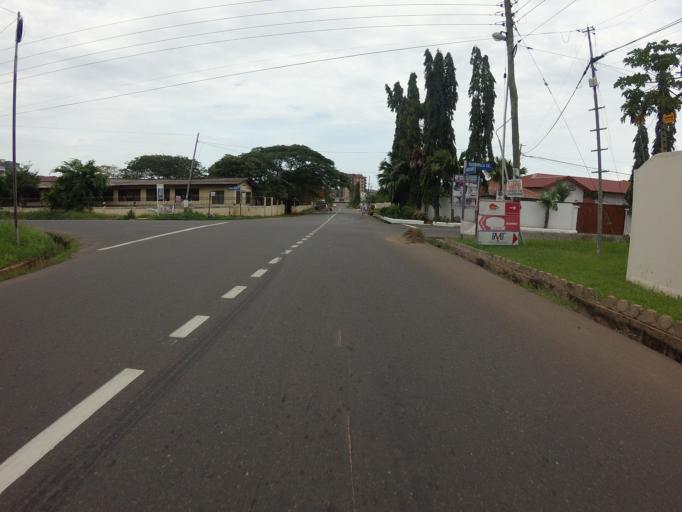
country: GH
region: Greater Accra
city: Dome
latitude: 5.6143
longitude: -0.2046
